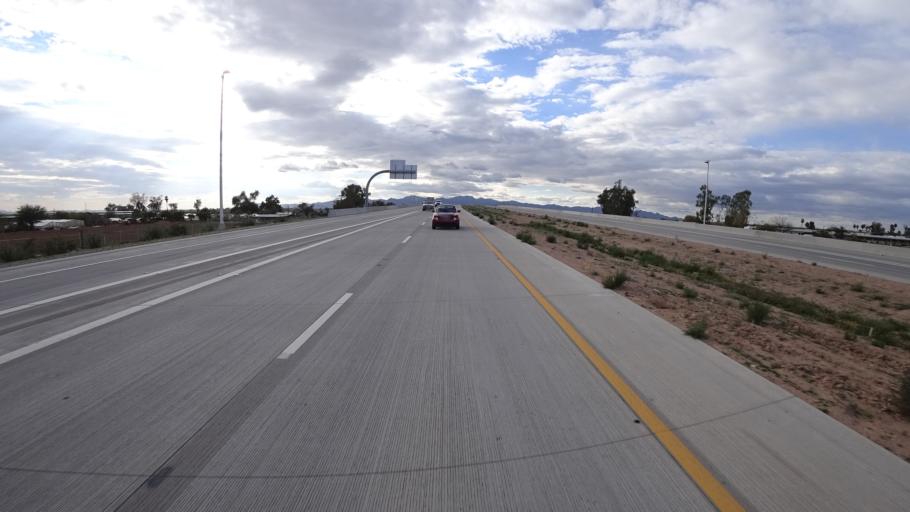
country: US
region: Arizona
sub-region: Maricopa County
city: Litchfield Park
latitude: 33.5577
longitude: -112.3638
